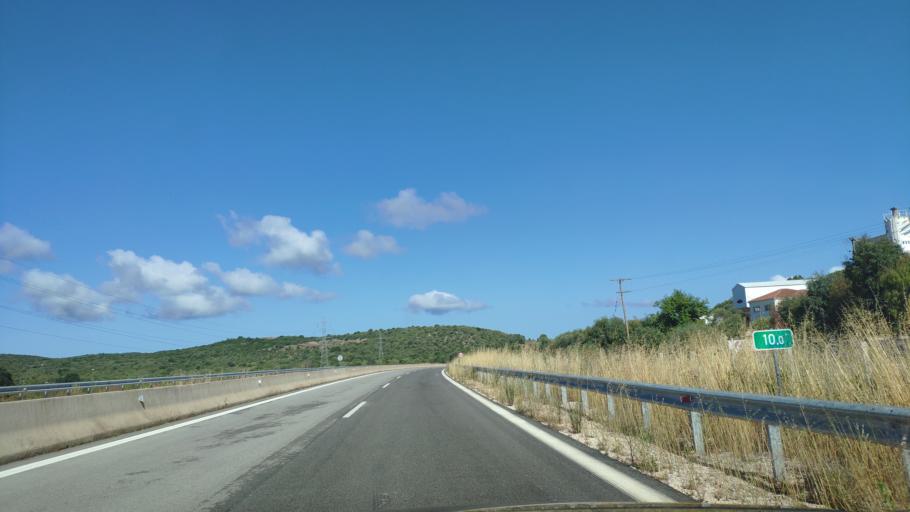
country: GR
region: West Greece
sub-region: Nomos Aitolias kai Akarnanias
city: Vonitsa
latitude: 38.9037
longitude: 20.8573
